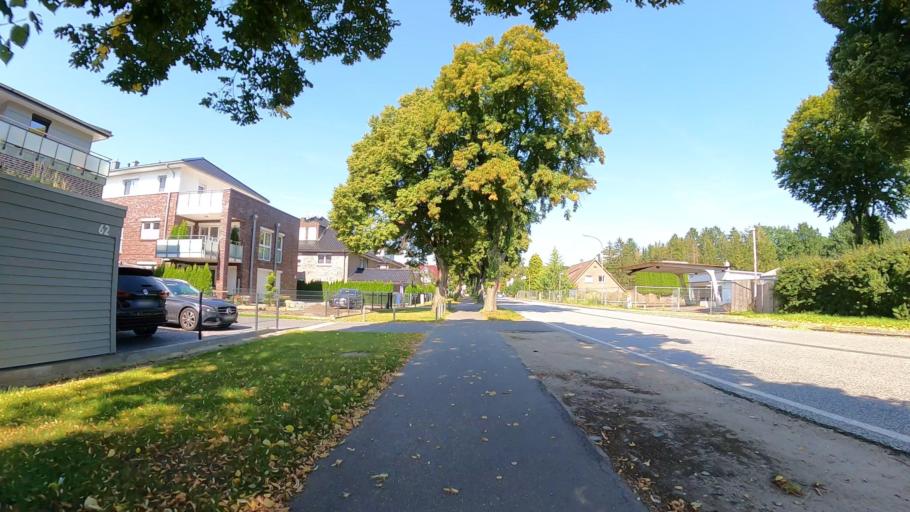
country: DE
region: Schleswig-Holstein
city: Bad Bramstedt
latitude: 53.9089
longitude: 9.8818
